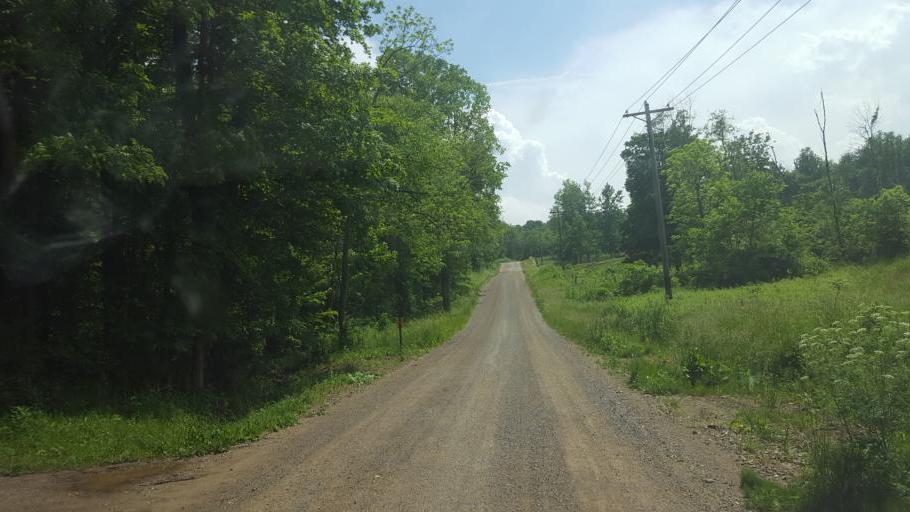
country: US
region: Ohio
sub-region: Knox County
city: Oak Hill
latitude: 40.3353
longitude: -82.2458
